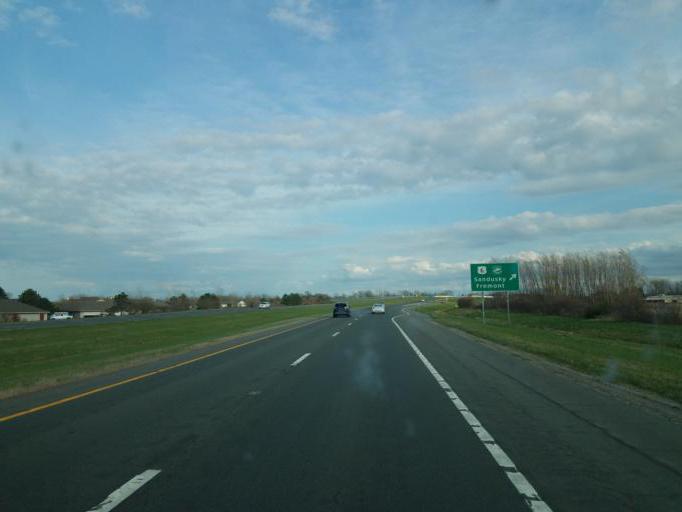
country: US
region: Ohio
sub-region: Erie County
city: Sandusky
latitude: 41.4456
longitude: -82.7850
